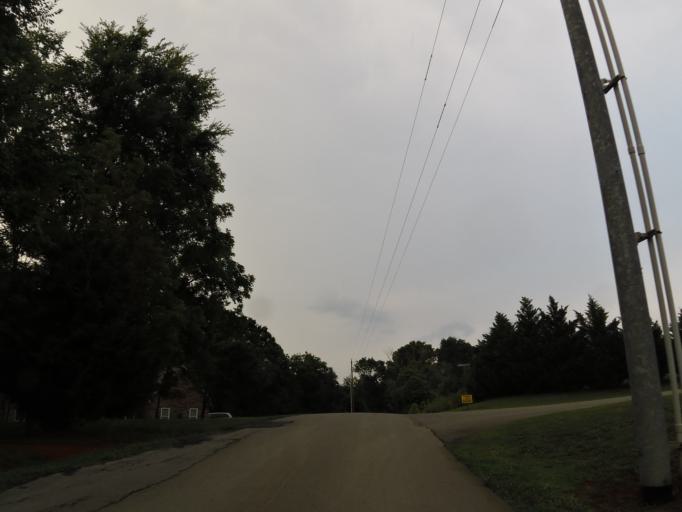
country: US
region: Tennessee
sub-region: Blount County
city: Wildwood
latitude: 35.8122
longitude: -83.8096
